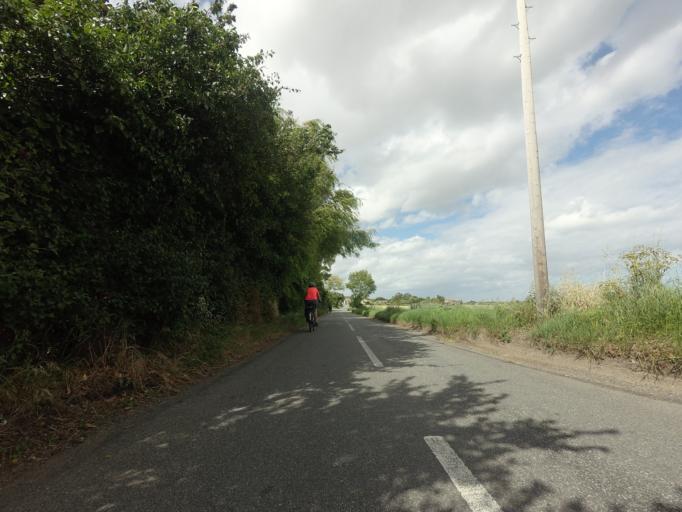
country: GB
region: England
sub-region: Medway
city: Allhallows
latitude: 51.4638
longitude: 0.6397
